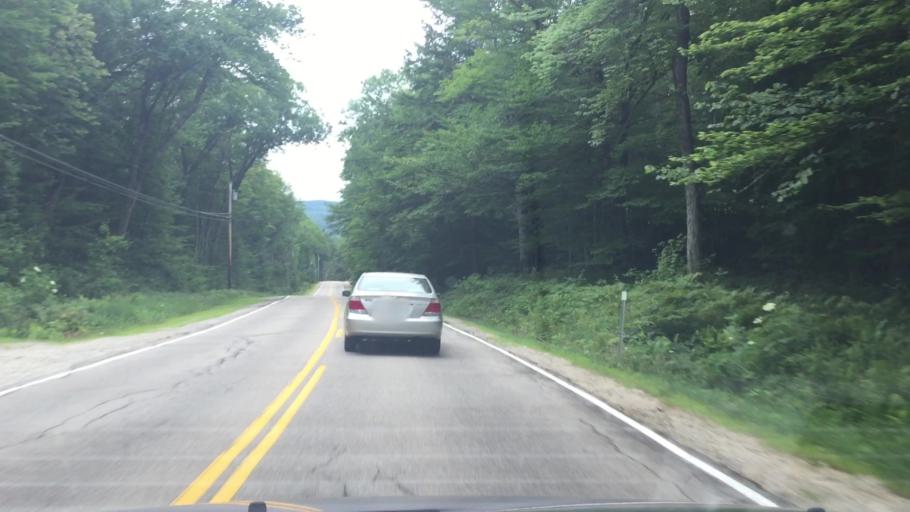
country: US
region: New Hampshire
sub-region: Carroll County
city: Conway
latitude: 43.9320
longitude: -71.0865
